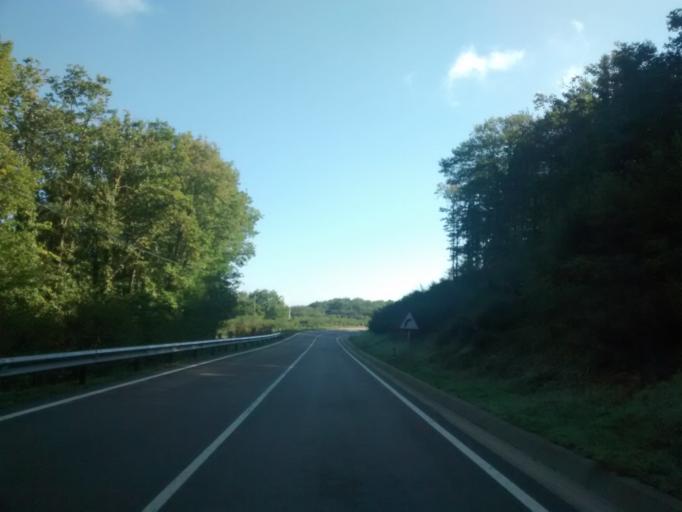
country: ES
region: Cantabria
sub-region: Provincia de Cantabria
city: Reinosa
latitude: 42.9740
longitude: -4.0991
